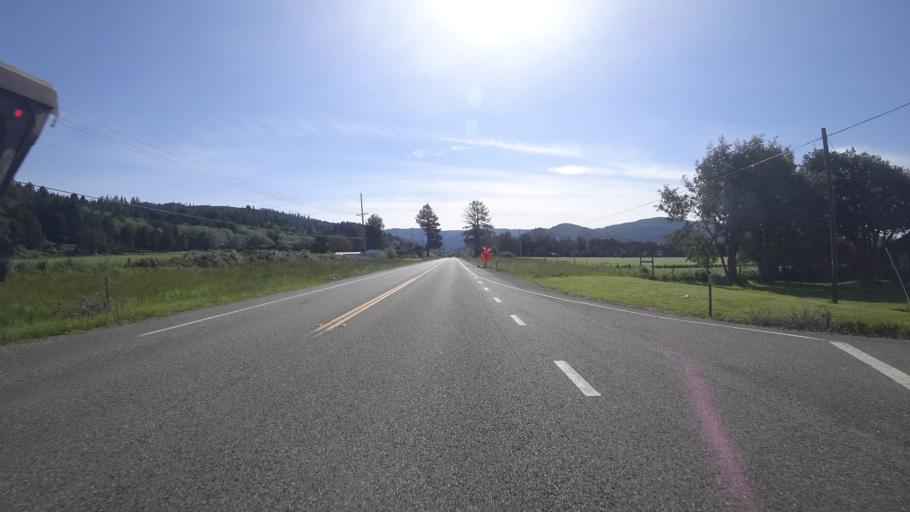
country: US
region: Oregon
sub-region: Curry County
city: Harbor
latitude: 41.9322
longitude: -124.1559
